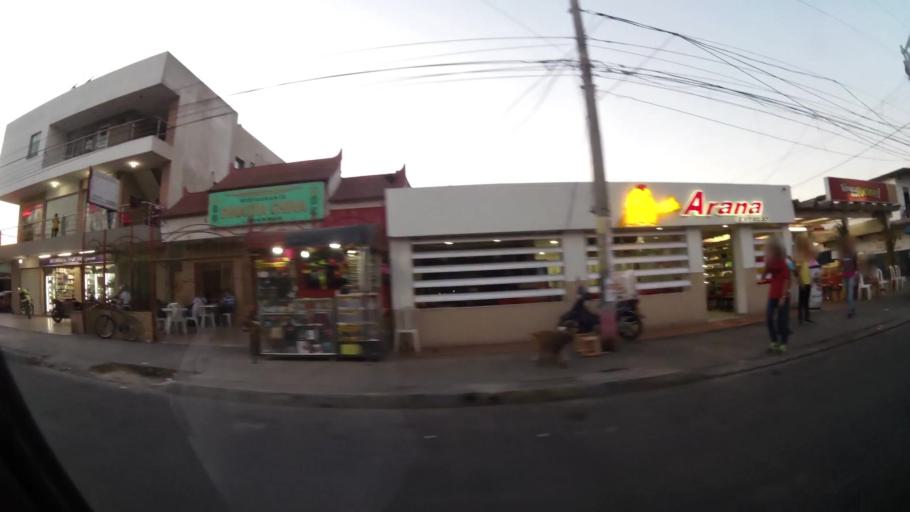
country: CO
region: Atlantico
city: Barranquilla
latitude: 10.9454
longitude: -74.7766
